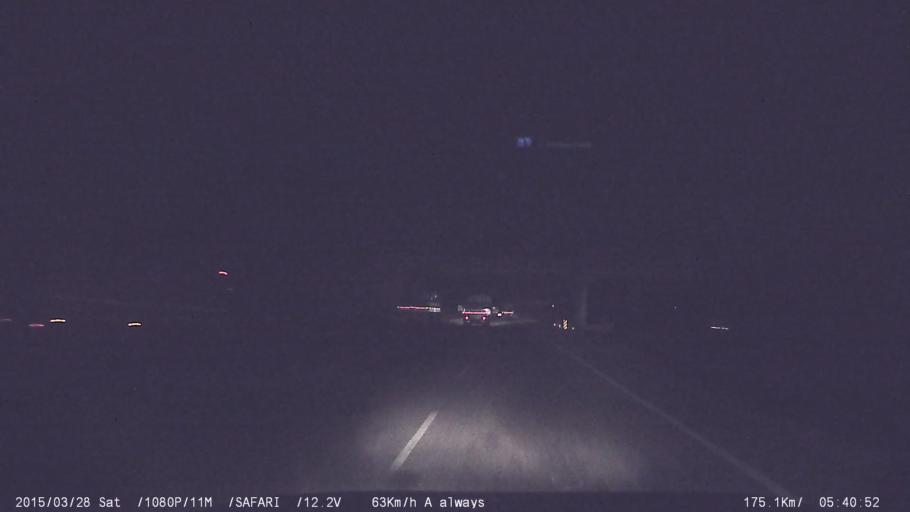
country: IN
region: Karnataka
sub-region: Bangalore Urban
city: Bangalore
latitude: 12.8503
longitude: 77.5834
